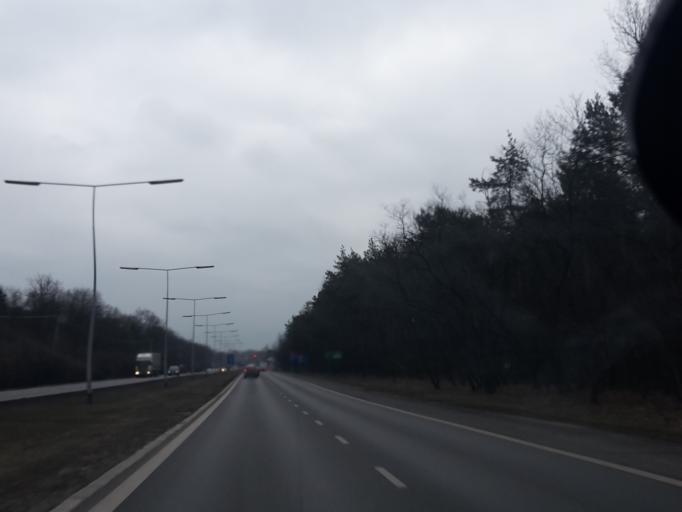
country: PL
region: Masovian Voivodeship
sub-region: Warszawa
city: Bielany
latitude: 52.3173
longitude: 20.9176
